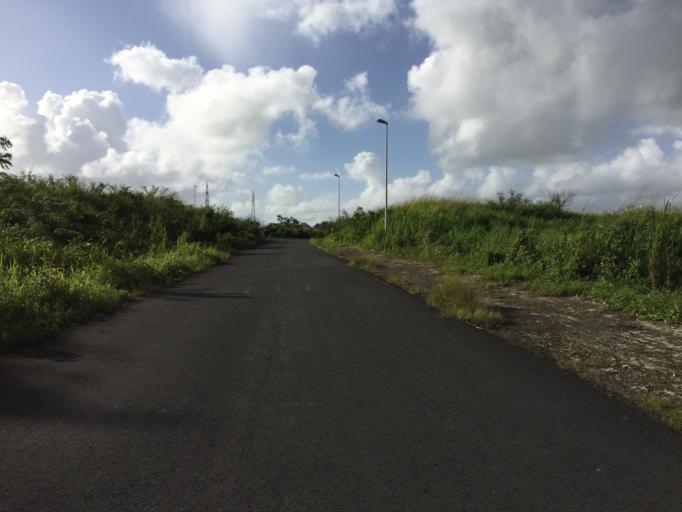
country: GP
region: Guadeloupe
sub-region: Guadeloupe
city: Baie-Mahault
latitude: 16.2410
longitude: -61.5744
